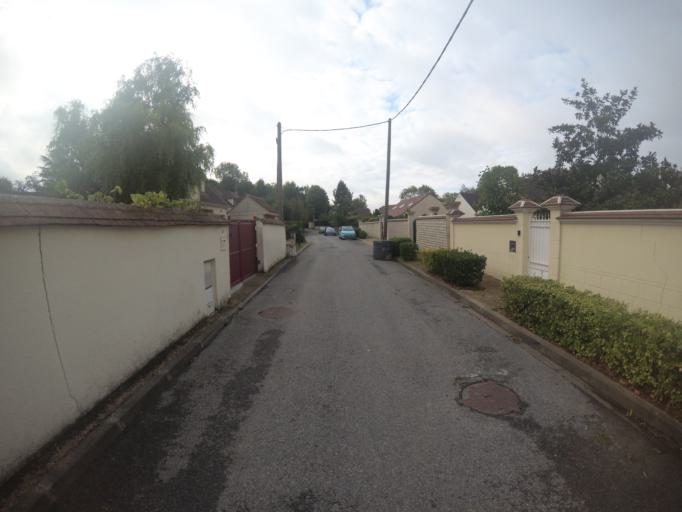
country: FR
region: Ile-de-France
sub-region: Departement de Seine-et-Marne
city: Dampmart
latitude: 48.8761
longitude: 2.7384
